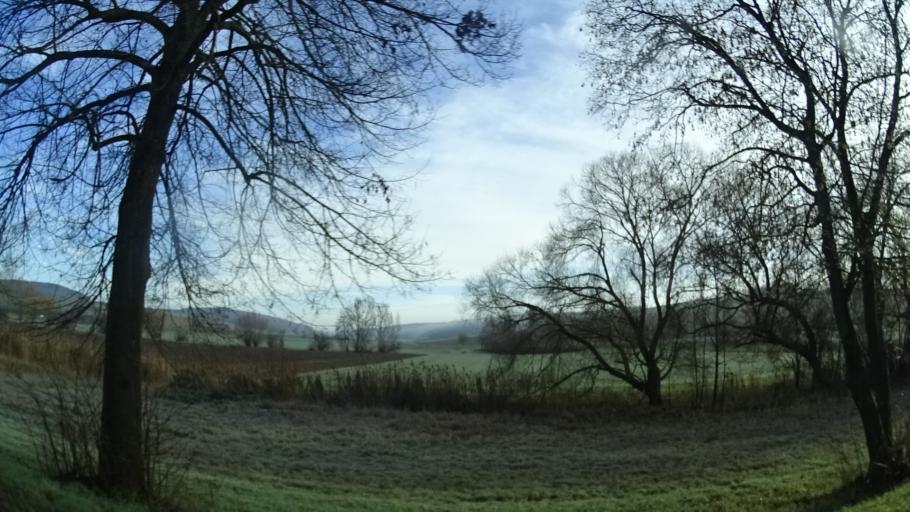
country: DE
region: Bavaria
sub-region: Regierungsbezirk Unterfranken
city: Waldbrunn
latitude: 49.7709
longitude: 9.7756
